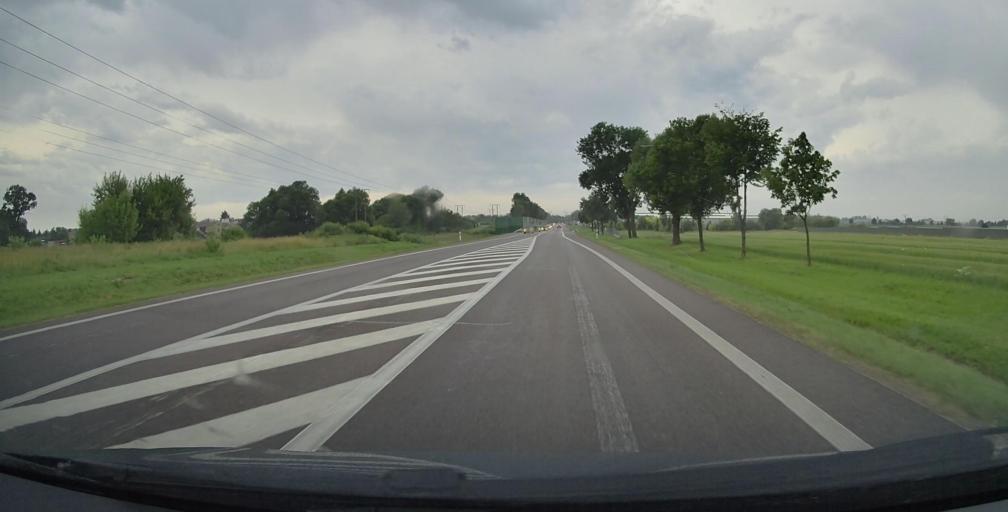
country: PL
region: Lublin Voivodeship
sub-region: Powiat bialski
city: Miedzyrzec Podlaski
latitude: 52.0002
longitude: 22.7769
